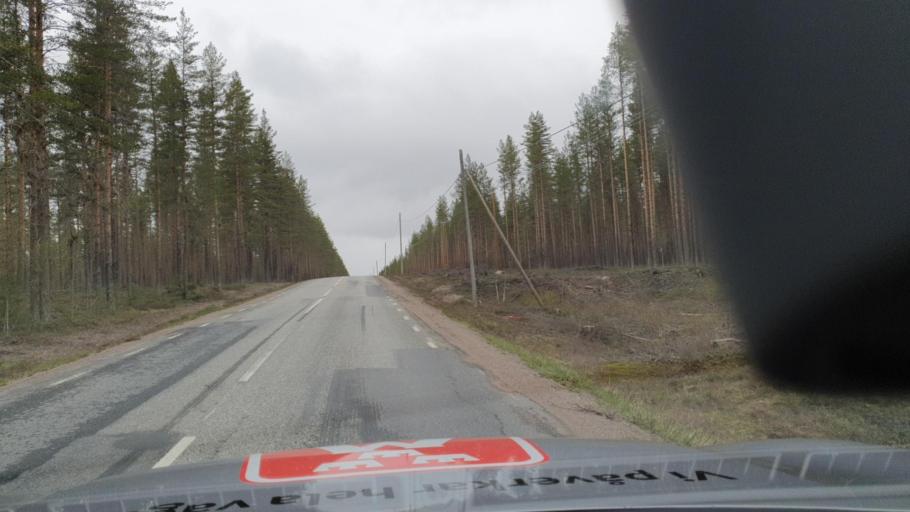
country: SE
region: Vaesternorrland
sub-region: Solleftea Kommun
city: Solleftea
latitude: 63.5992
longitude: 17.5442
